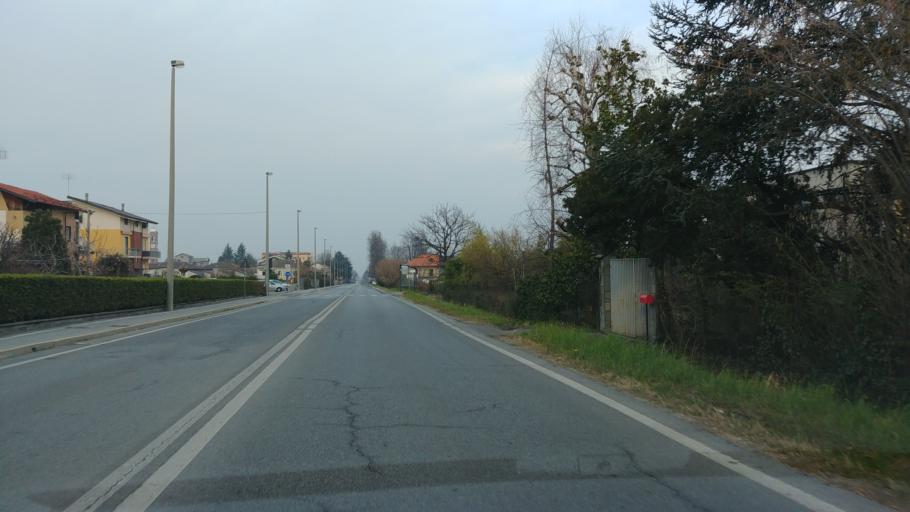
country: IT
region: Piedmont
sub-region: Provincia di Cuneo
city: Borgo San Dalmazzo
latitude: 44.3607
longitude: 7.5183
